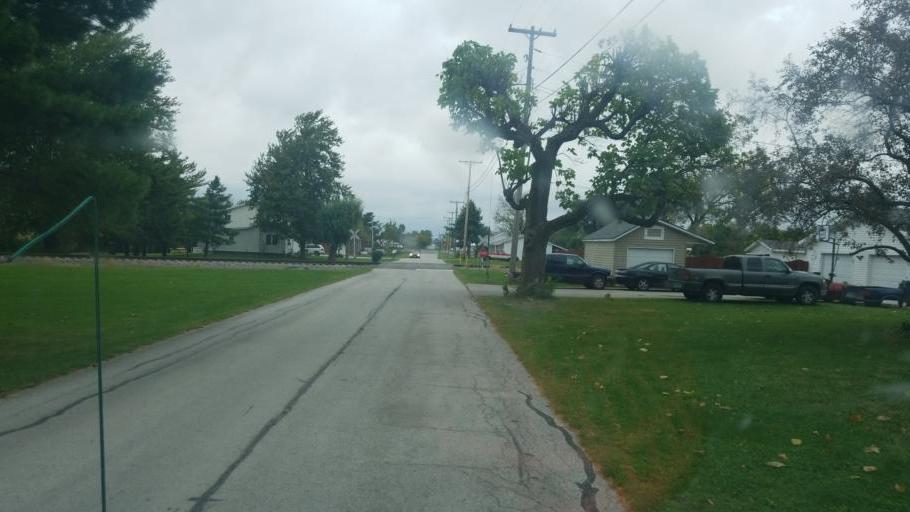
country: US
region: Ohio
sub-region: Seneca County
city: Fostoria
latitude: 41.1100
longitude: -83.5163
